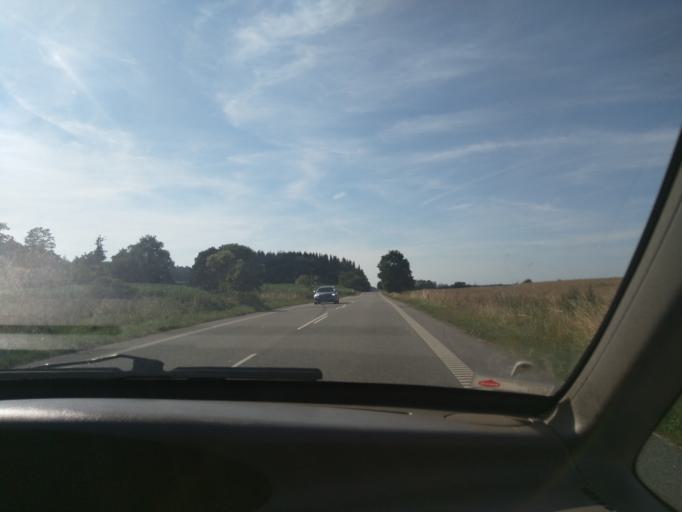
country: DK
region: Central Jutland
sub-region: Viborg Kommune
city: Bjerringbro
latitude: 56.4444
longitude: 9.6201
